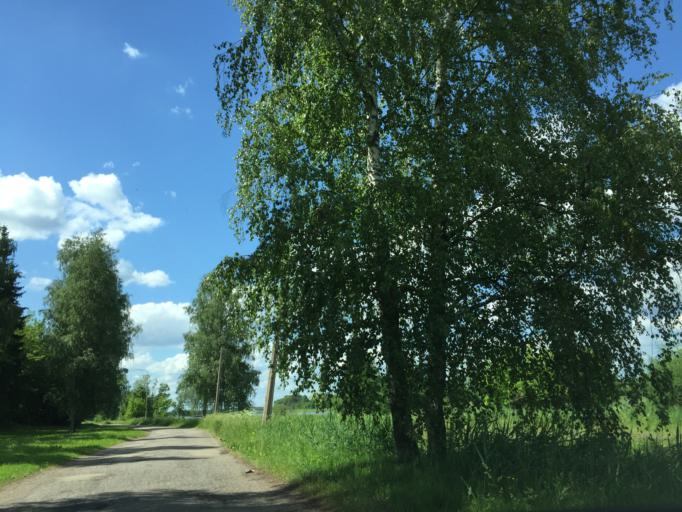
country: LV
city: Tireli
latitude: 56.8028
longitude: 23.6082
